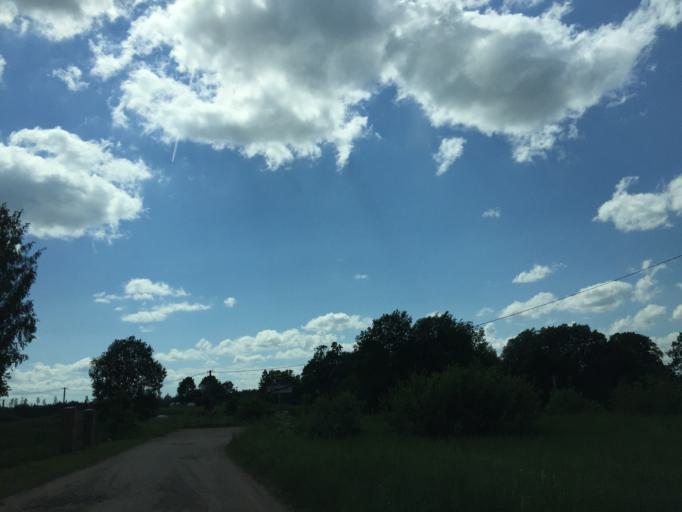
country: LV
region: Priekuli
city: Priekuli
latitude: 57.2598
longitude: 25.4246
